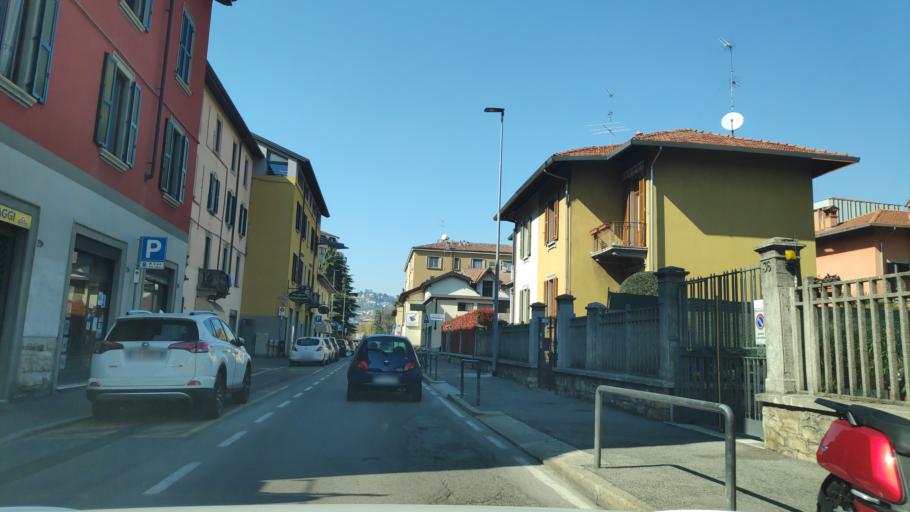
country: IT
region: Lombardy
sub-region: Provincia di Bergamo
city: Bergamo
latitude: 45.6850
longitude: 9.6750
